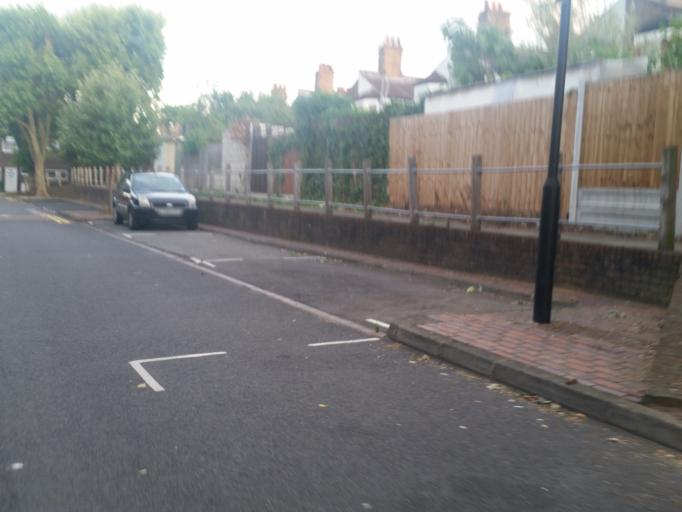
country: GB
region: England
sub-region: Greater London
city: Harringay
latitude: 51.5900
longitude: -0.0963
